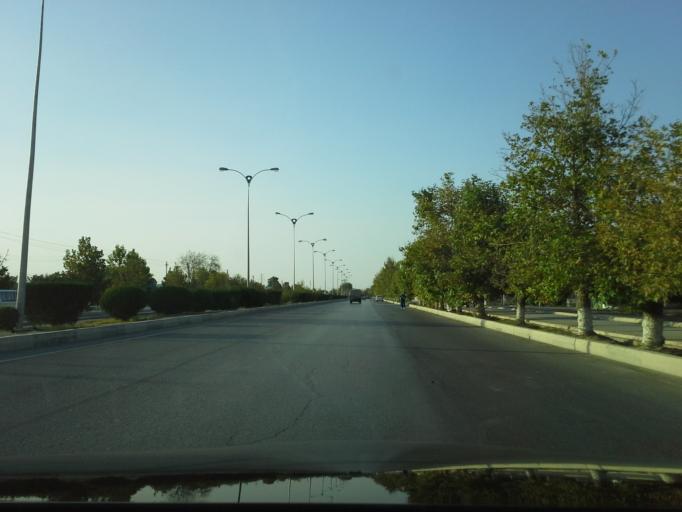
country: TM
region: Ahal
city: Abadan
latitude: 38.0325
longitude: 58.1917
